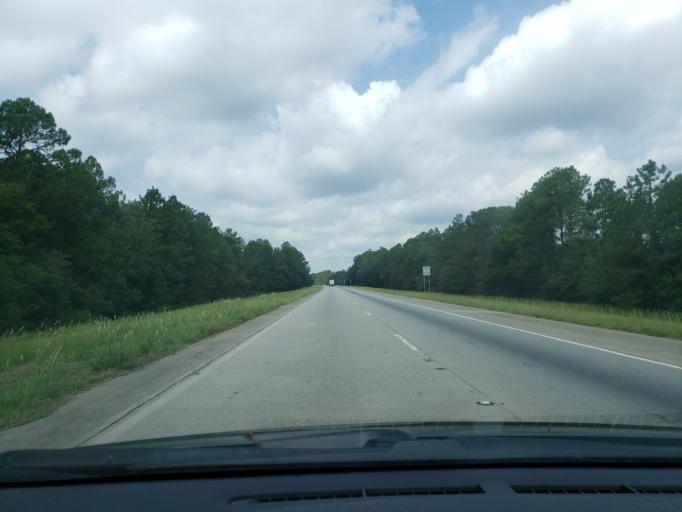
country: US
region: Georgia
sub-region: Treutlen County
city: Soperton
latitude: 32.4226
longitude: -82.4187
